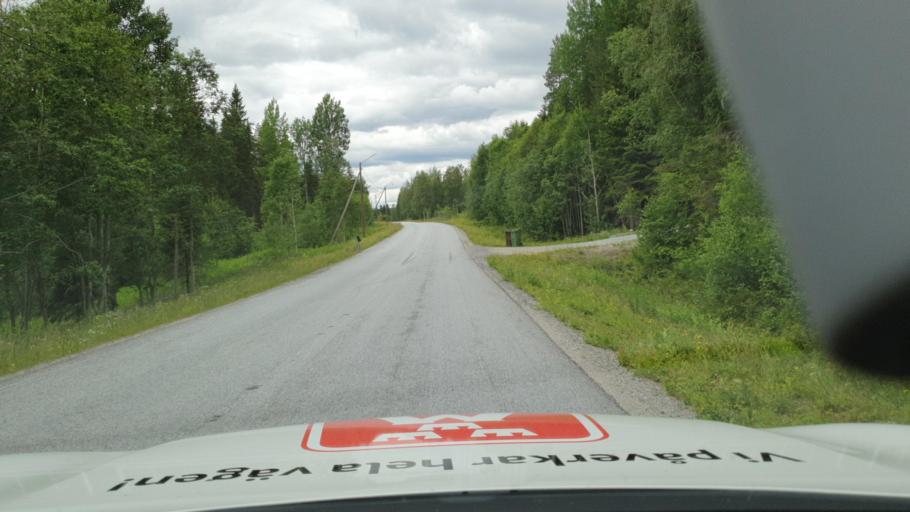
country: SE
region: Vaesterbotten
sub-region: Bjurholms Kommun
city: Bjurholm
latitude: 63.7823
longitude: 19.2116
